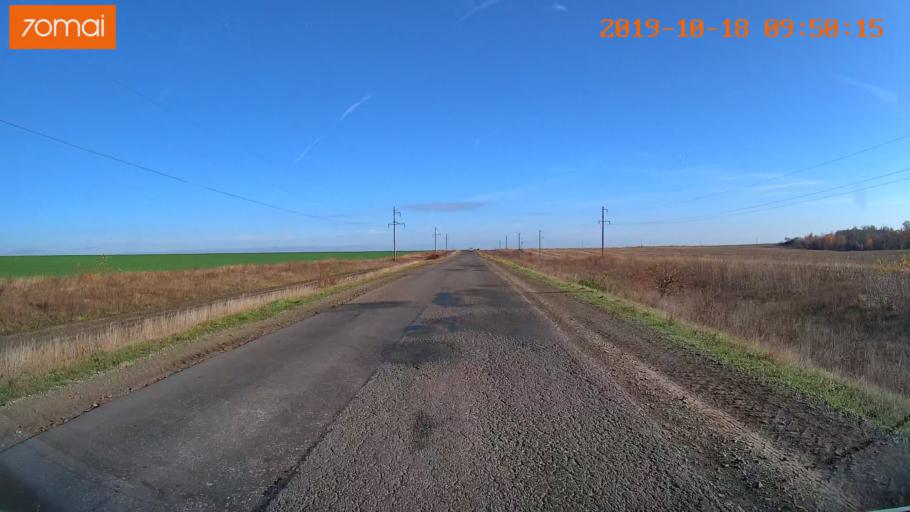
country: RU
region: Tula
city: Kazachka
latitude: 53.3267
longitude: 38.2748
